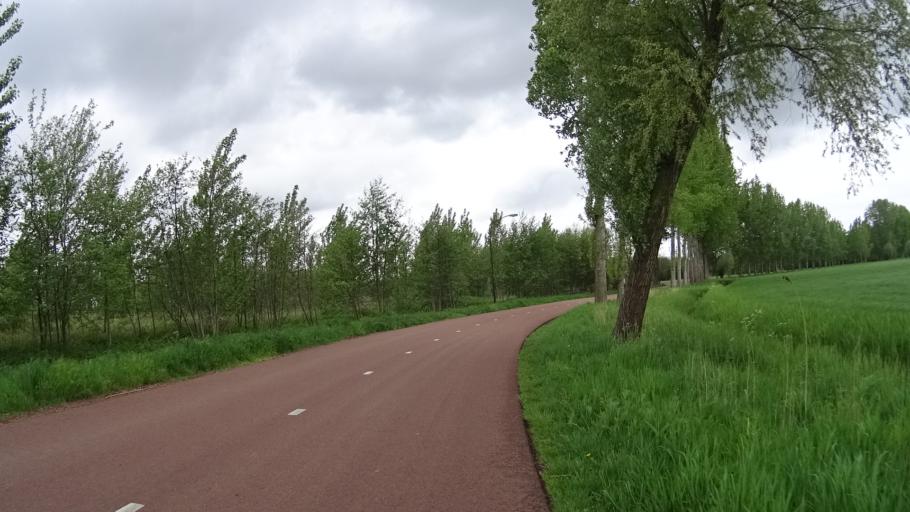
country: NL
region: North Brabant
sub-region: Gemeente Veghel
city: Eerde
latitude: 51.6157
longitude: 5.4988
